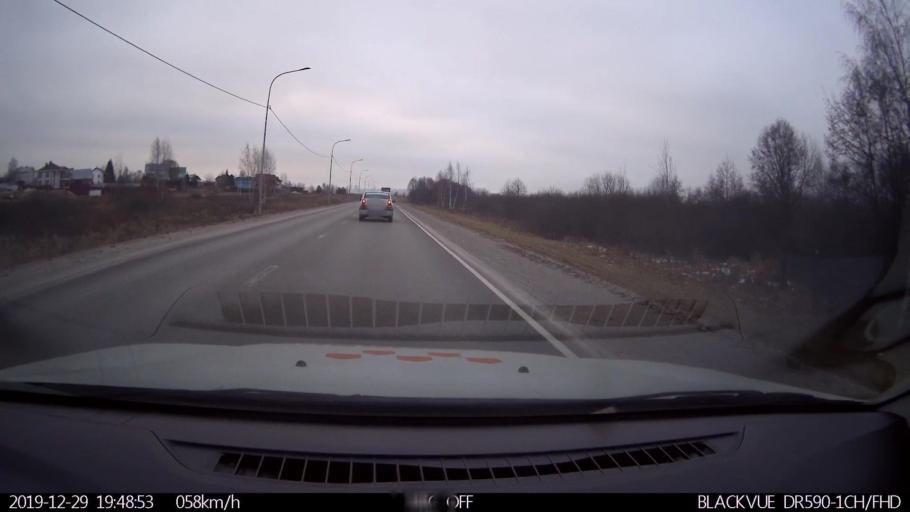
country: RU
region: Nizjnij Novgorod
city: Neklyudovo
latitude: 56.3821
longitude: 44.0103
